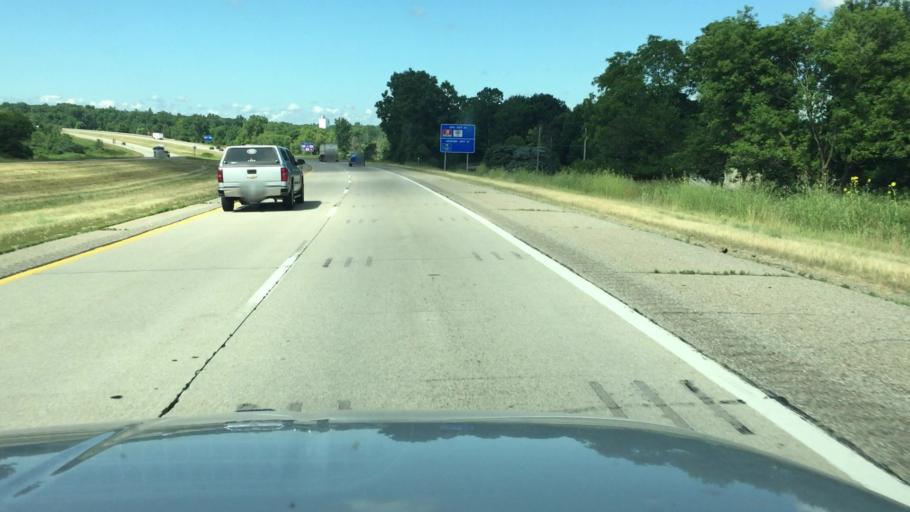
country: US
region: Michigan
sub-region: Eaton County
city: Charlotte
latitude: 42.5878
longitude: -84.8084
